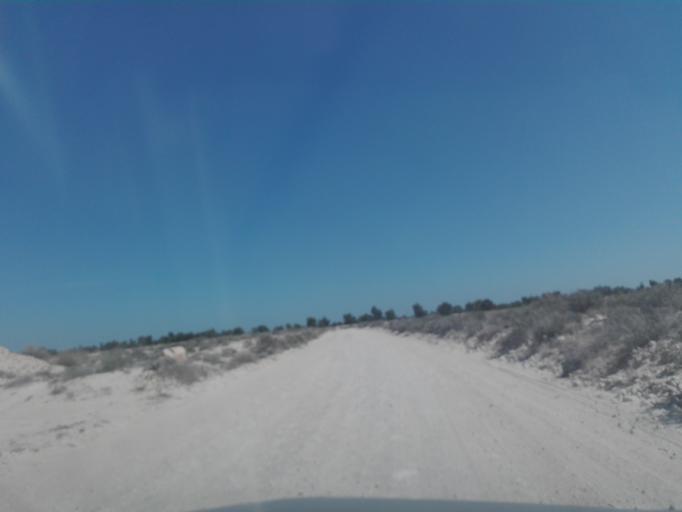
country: TN
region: Qabis
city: Gabes
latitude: 33.8703
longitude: 10.0115
